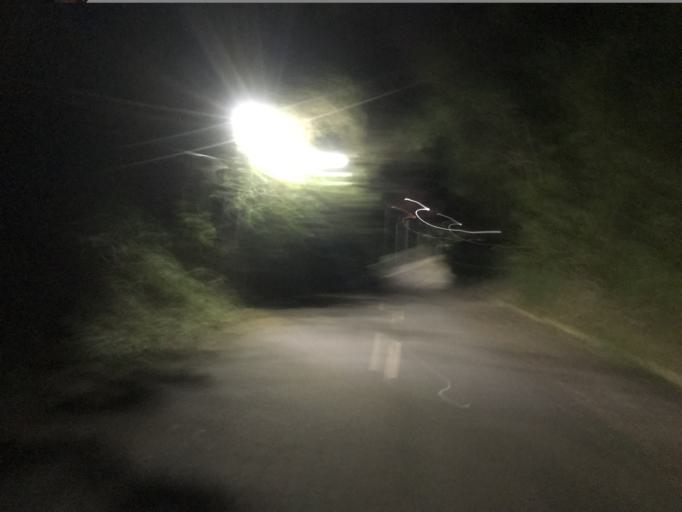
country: TW
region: Taiwan
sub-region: Hsinchu
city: Hsinchu
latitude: 24.7540
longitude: 120.9446
